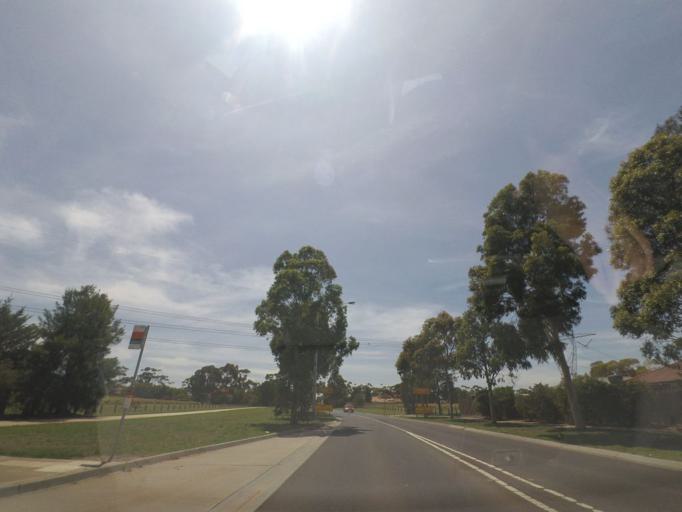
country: AU
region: Victoria
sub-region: Hume
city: Roxburgh Park
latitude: -37.6274
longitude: 144.9219
